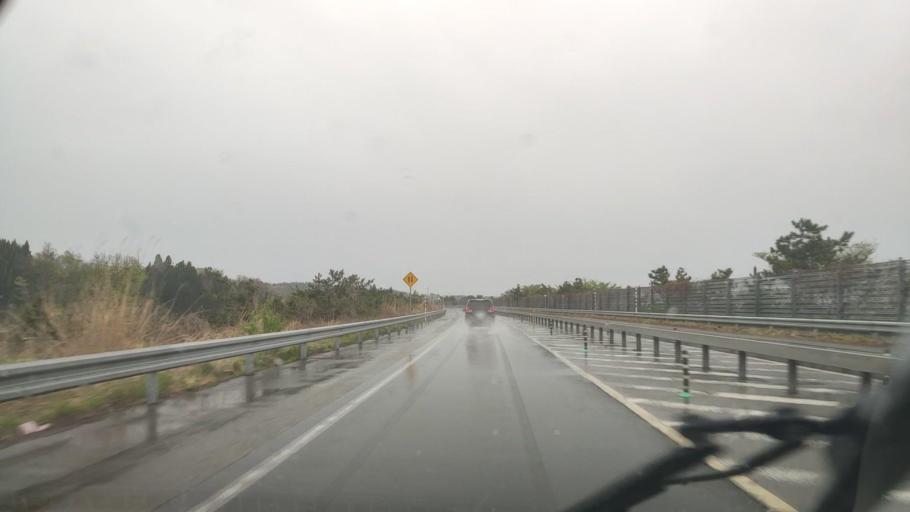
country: JP
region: Akita
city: Noshiromachi
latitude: 40.1808
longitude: 140.0638
